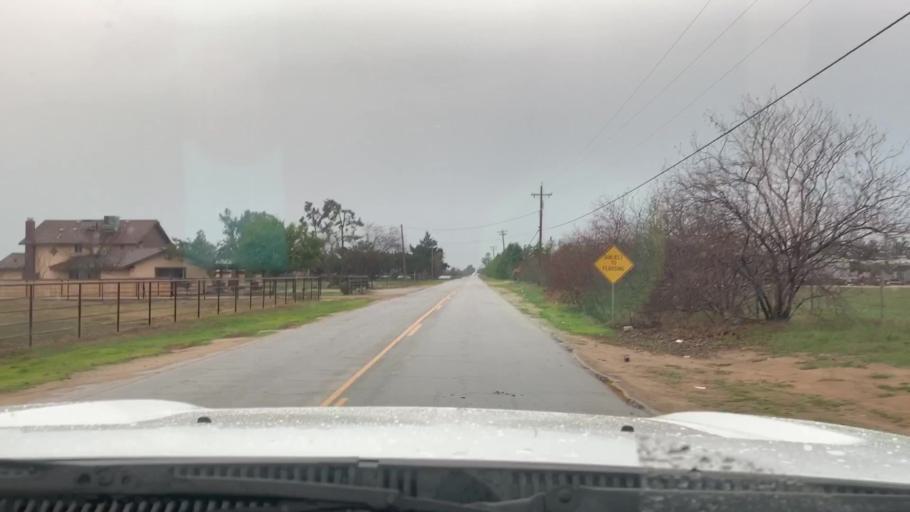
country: US
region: California
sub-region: Kern County
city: Shafter
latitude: 35.4780
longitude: -119.2611
